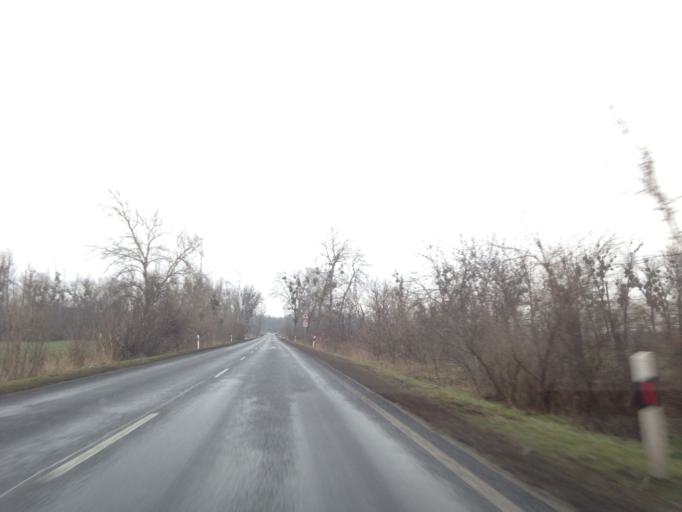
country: HU
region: Komarom-Esztergom
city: Dunaalmas
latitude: 47.7002
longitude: 18.2998
